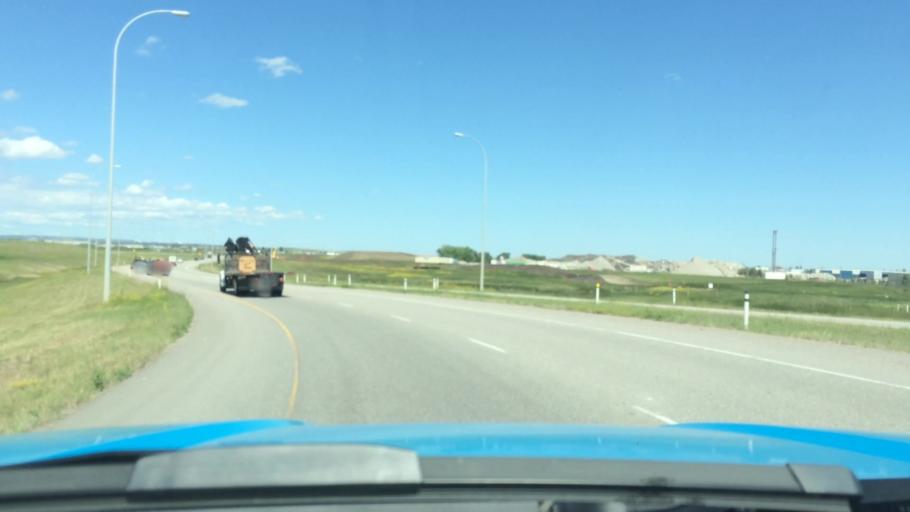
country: CA
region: Alberta
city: Chestermere
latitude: 50.9806
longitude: -113.9151
